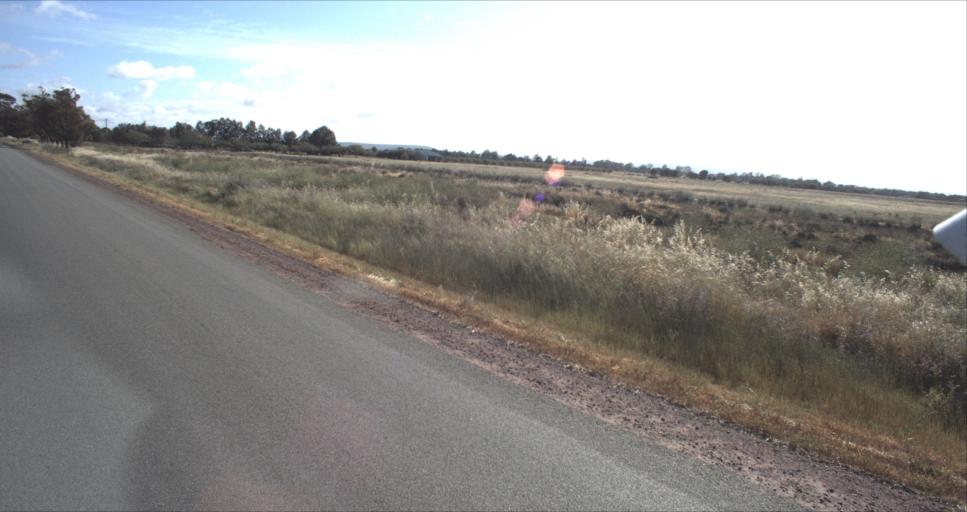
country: AU
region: New South Wales
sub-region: Leeton
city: Leeton
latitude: -34.5230
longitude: 146.3902
